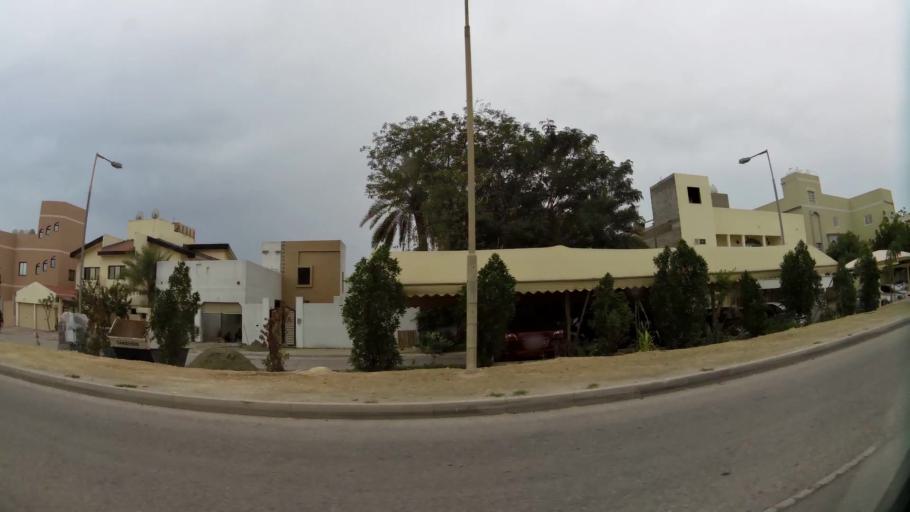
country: BH
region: Central Governorate
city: Madinat Hamad
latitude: 26.1127
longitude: 50.4988
